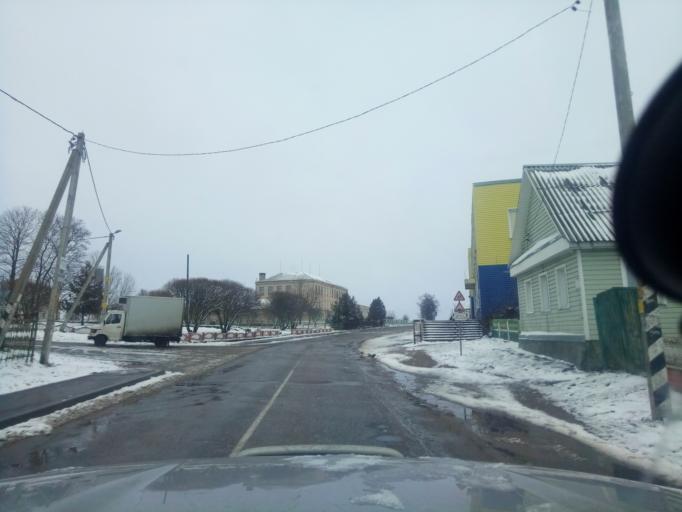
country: BY
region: Minsk
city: Tsimkavichy
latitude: 53.0717
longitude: 26.9909
